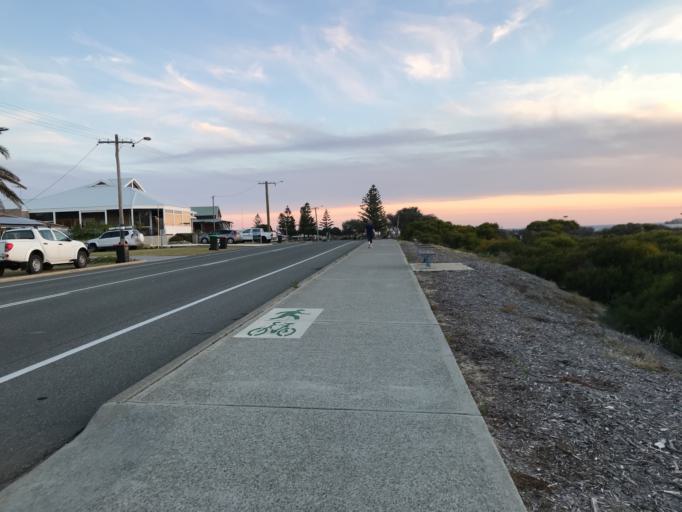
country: AU
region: Western Australia
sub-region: Rockingham
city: Shoalwater
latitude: -32.3024
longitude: 115.7030
